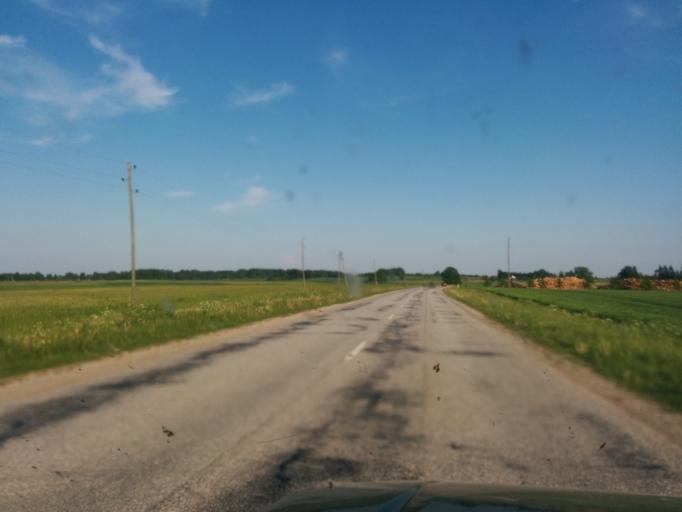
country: LV
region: Talsu Rajons
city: Talsi
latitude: 57.2966
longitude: 22.5635
